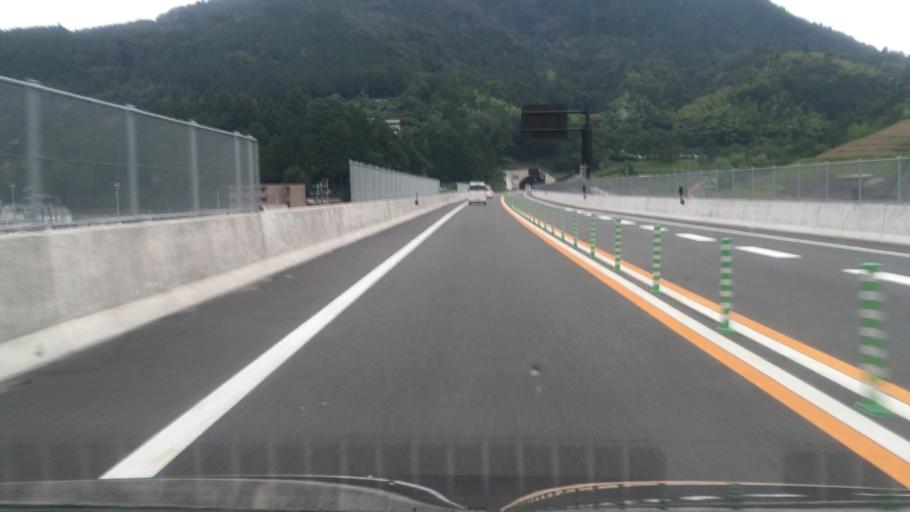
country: JP
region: Hyogo
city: Toyooka
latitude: 35.3929
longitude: 134.7456
